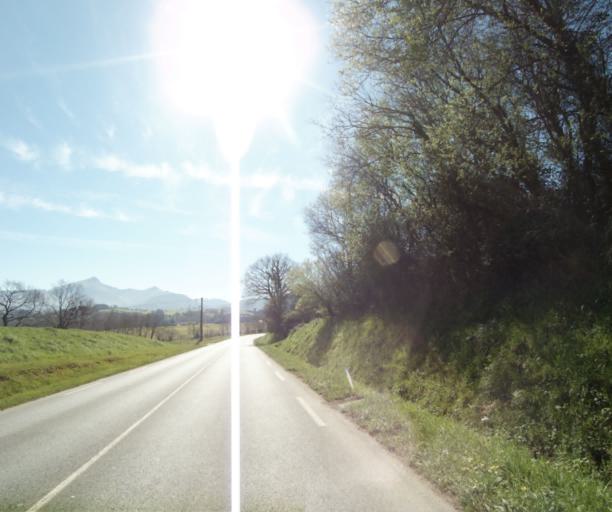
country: FR
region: Aquitaine
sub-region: Departement des Pyrenees-Atlantiques
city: Urrugne
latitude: 43.3566
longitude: -1.6913
